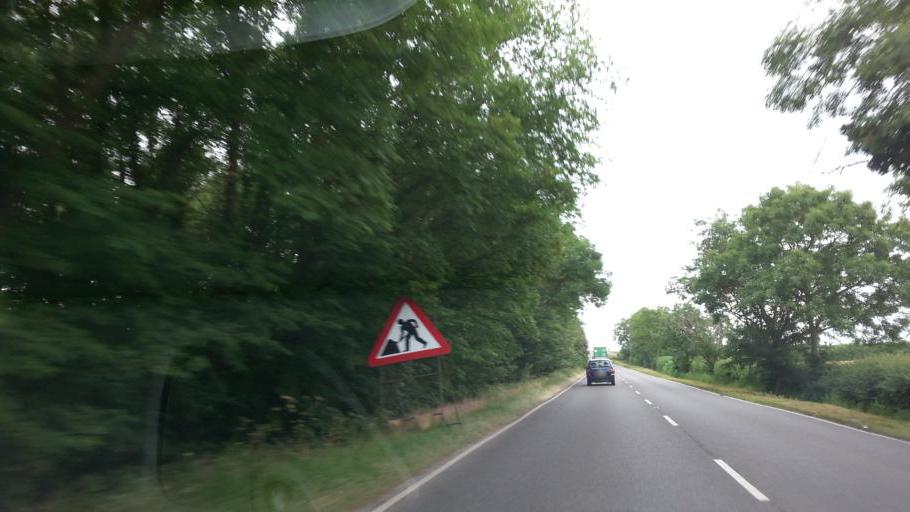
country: GB
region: England
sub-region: Cambridgeshire
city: Papworth Everard
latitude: 52.2855
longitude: -0.1445
